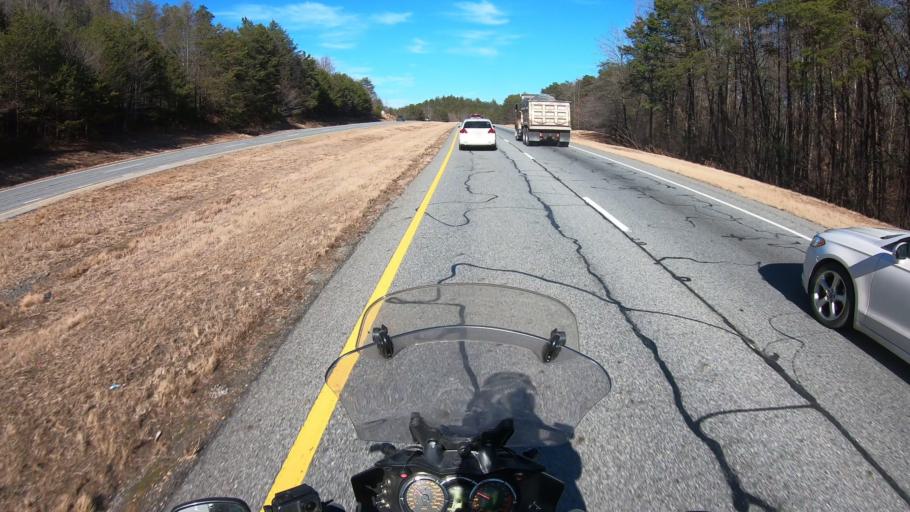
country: US
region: Georgia
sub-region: Gilmer County
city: Ellijay
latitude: 34.7527
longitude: -84.4071
